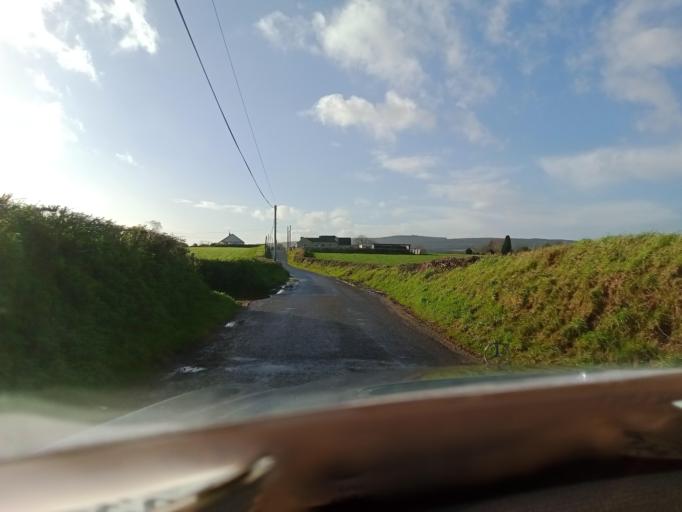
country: IE
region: Munster
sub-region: Waterford
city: Portlaw
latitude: 52.3272
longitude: -7.2853
